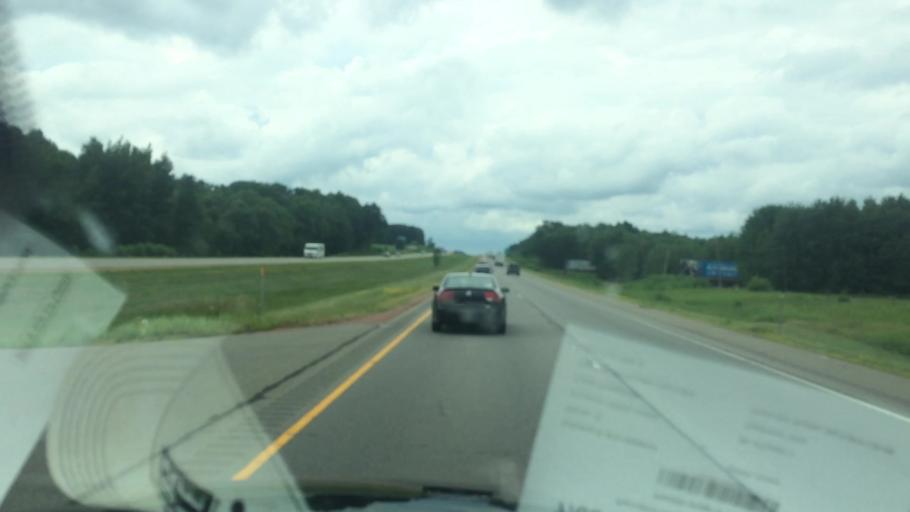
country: US
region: Wisconsin
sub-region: Marathon County
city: Mosinee
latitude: 44.7607
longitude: -89.6798
